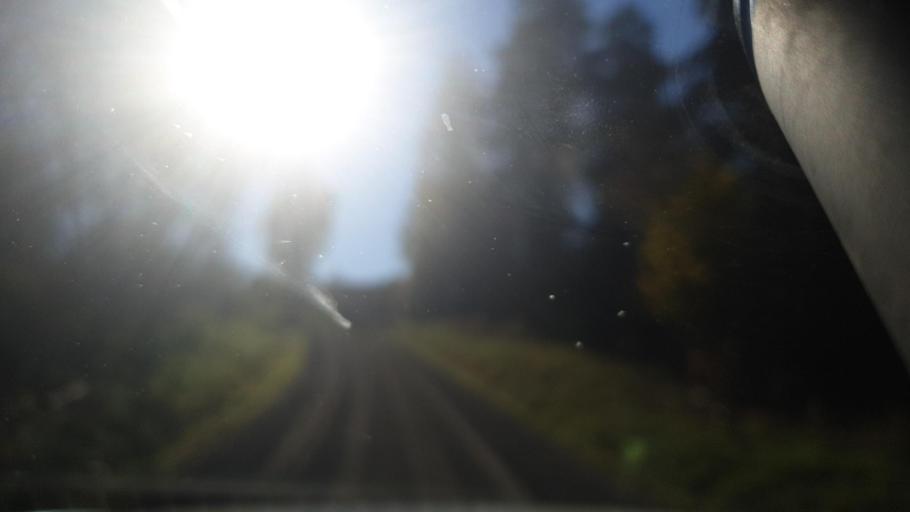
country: SE
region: Vaermland
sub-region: Grums Kommun
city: Grums
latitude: 59.4788
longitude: 12.9288
